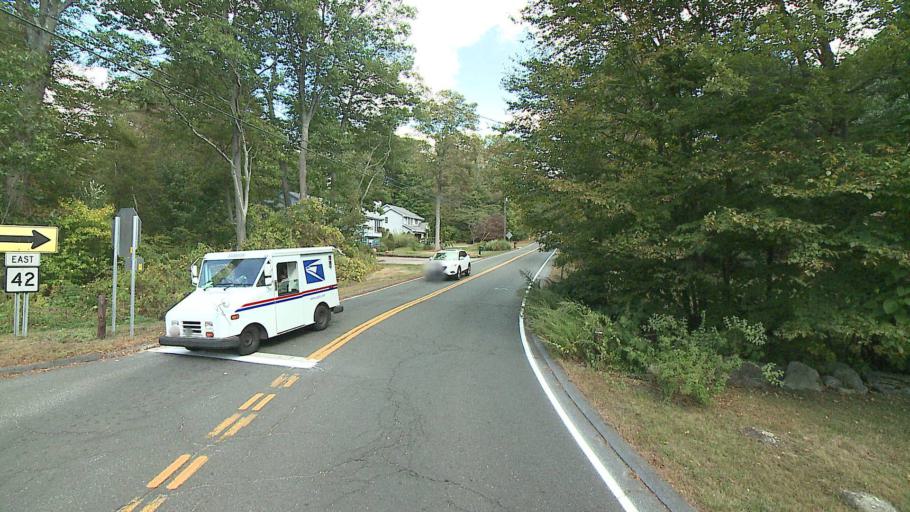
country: US
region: Connecticut
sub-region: New Haven County
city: Naugatuck
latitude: 41.4456
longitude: -73.0364
